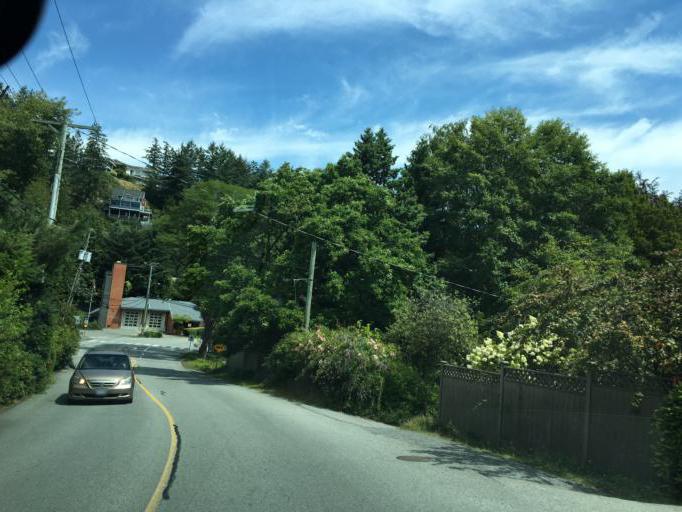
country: CA
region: British Columbia
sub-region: Greater Vancouver Regional District
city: Bowen Island
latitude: 49.3404
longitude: -123.2599
